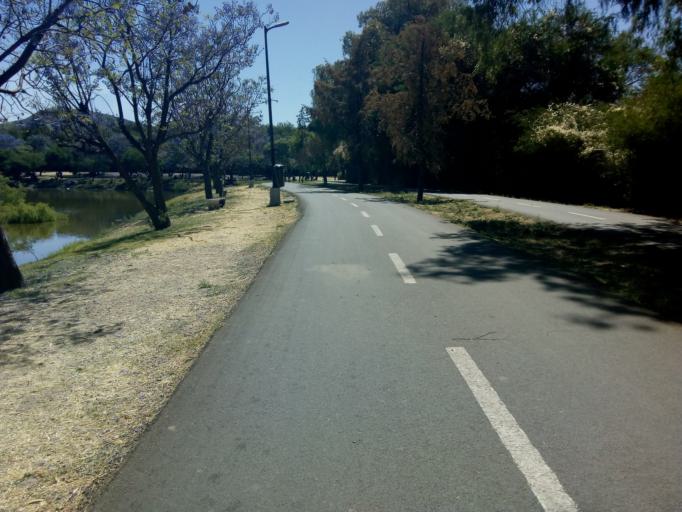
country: MX
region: Guanajuato
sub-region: Leon
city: La Ermita
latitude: 21.1781
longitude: -101.6974
